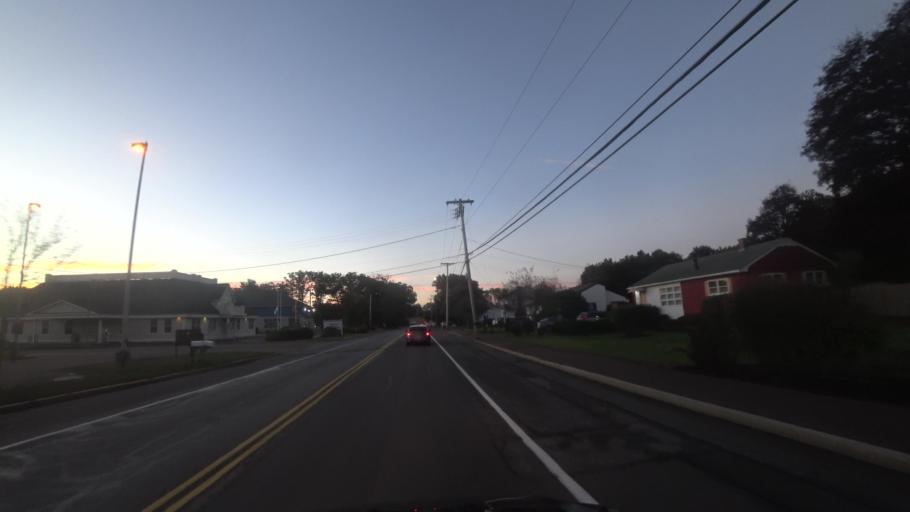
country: US
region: Massachusetts
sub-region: Middlesex County
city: Melrose
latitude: 42.4816
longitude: -71.0421
